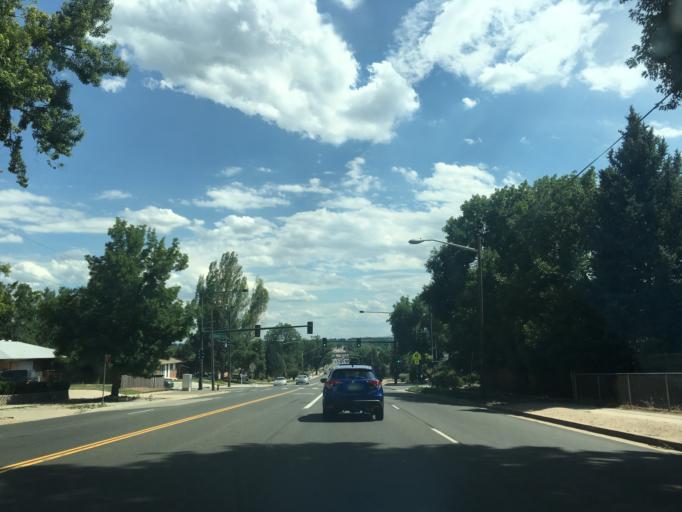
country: US
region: Colorado
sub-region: Arapahoe County
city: Sheridan
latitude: 39.6635
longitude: -105.0534
